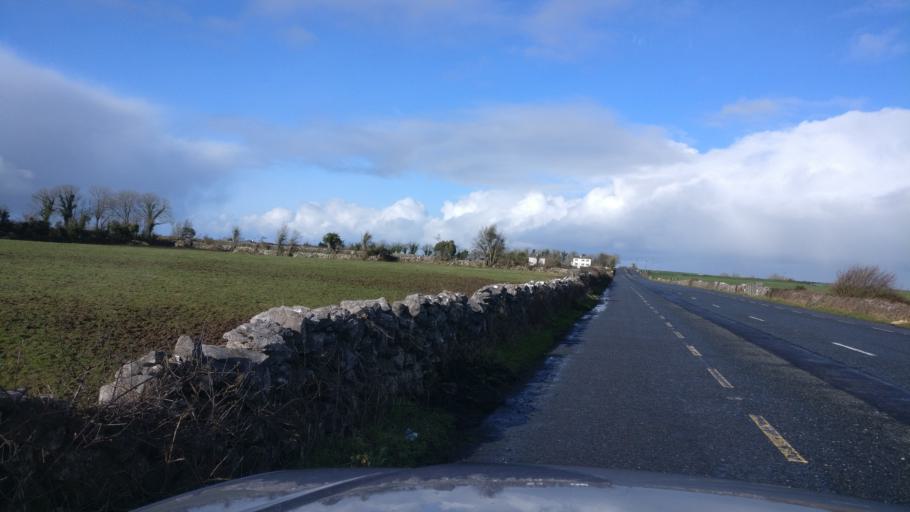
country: IE
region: Connaught
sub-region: County Galway
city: Athenry
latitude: 53.2431
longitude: -8.7577
